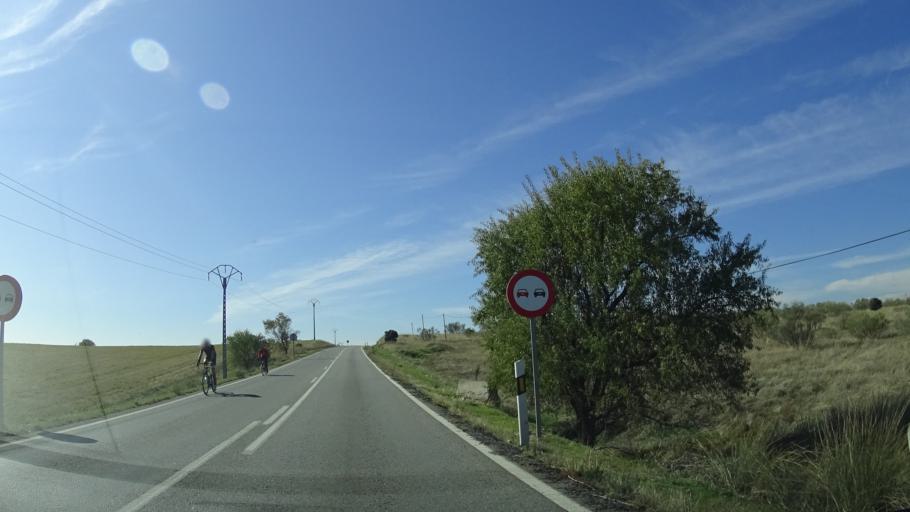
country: ES
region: Madrid
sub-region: Provincia de Madrid
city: Las Rozas de Madrid
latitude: 40.4982
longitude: -3.9007
